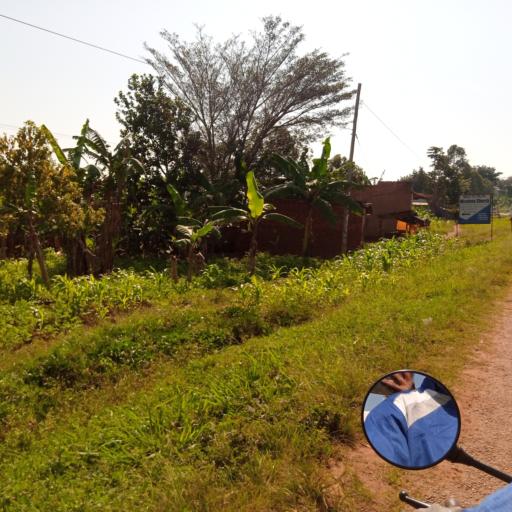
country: UG
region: Central Region
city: Masaka
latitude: -0.3779
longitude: 31.7106
